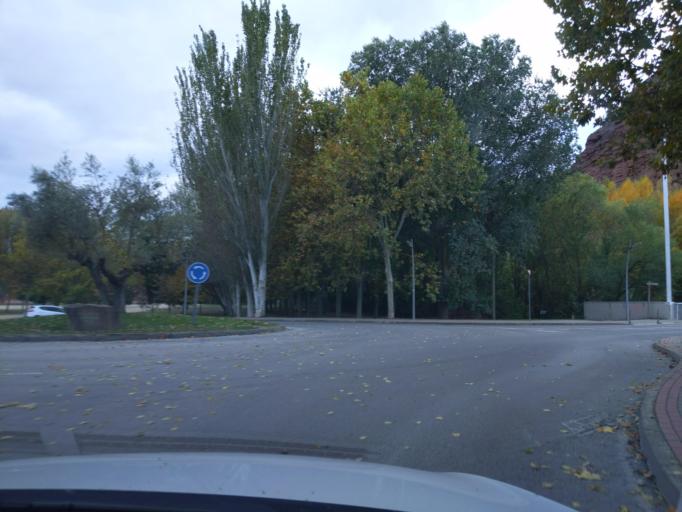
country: ES
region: La Rioja
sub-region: Provincia de La Rioja
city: Najera
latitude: 42.4130
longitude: -2.7330
